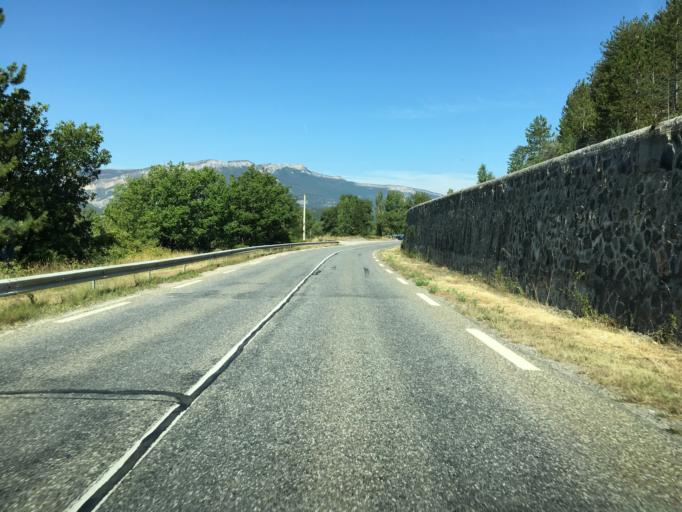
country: FR
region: Provence-Alpes-Cote d'Azur
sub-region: Departement des Hautes-Alpes
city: Laragne-Monteglin
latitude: 44.3411
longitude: 5.7773
